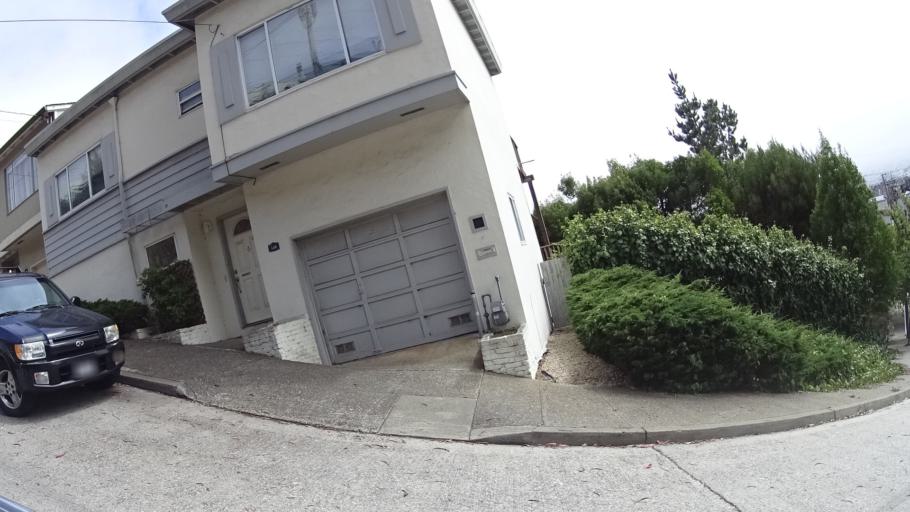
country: US
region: California
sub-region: San Mateo County
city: Daly City
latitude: 37.7364
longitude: -122.4500
